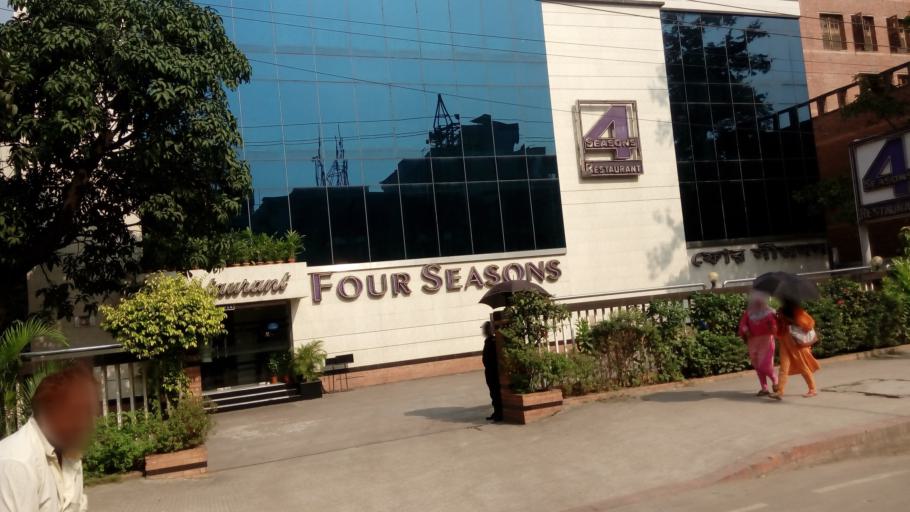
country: BD
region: Dhaka
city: Azimpur
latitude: 23.7514
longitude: 90.3677
